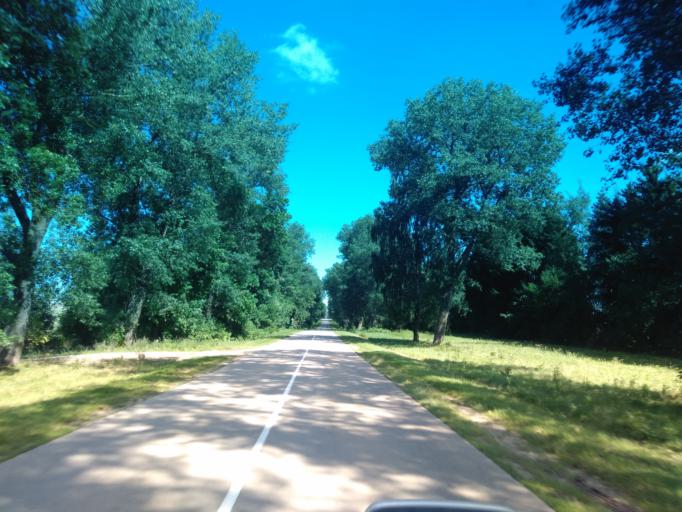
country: BY
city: Fanipol
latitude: 53.6645
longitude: 27.3327
